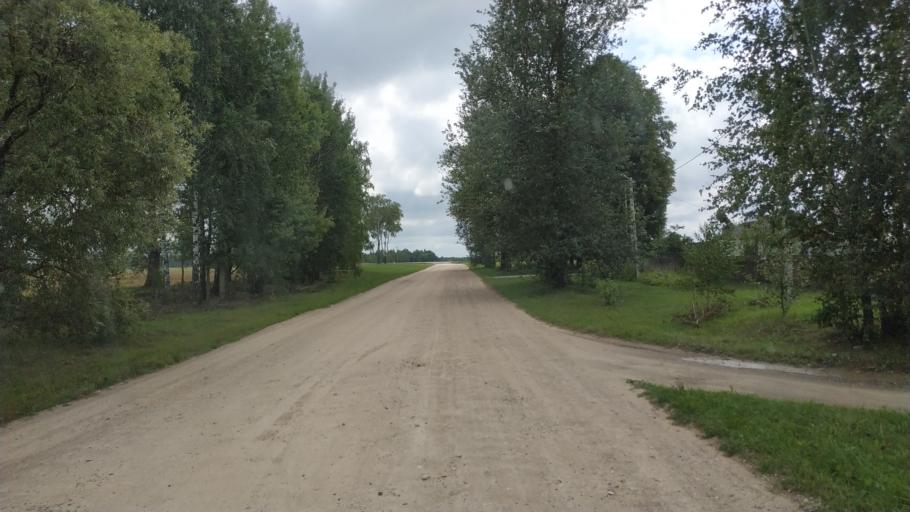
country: BY
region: Mogilev
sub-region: Mahilyowski Rayon
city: Kadino
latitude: 53.8462
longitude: 30.4756
